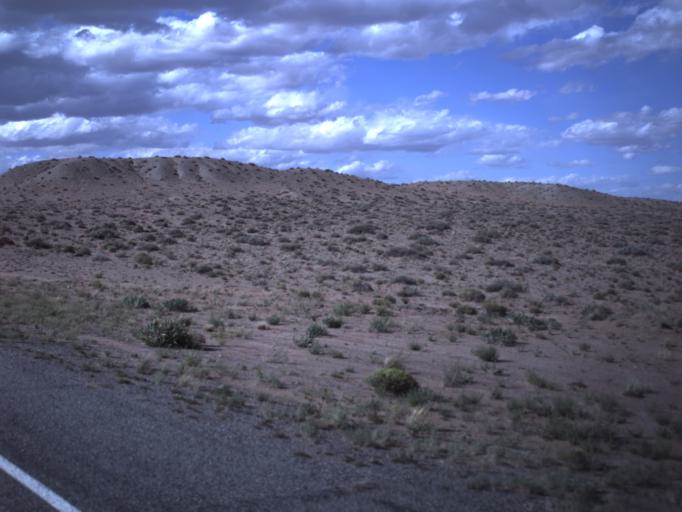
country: US
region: Utah
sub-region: Emery County
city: Ferron
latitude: 38.3377
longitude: -110.6880
